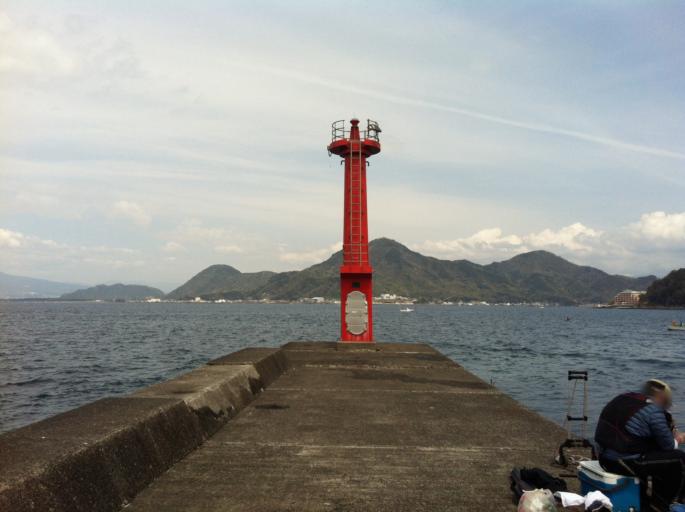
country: JP
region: Shizuoka
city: Numazu
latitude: 35.0277
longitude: 138.8776
